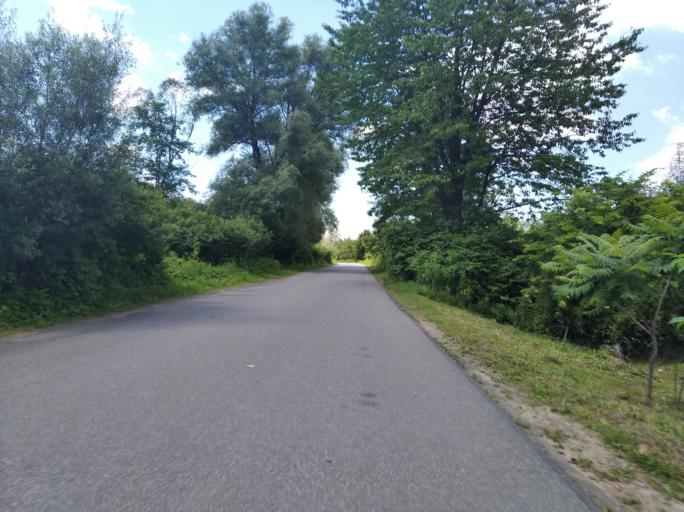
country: PL
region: Subcarpathian Voivodeship
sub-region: Powiat brzozowski
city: Dydnia
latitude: 49.7127
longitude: 22.2115
